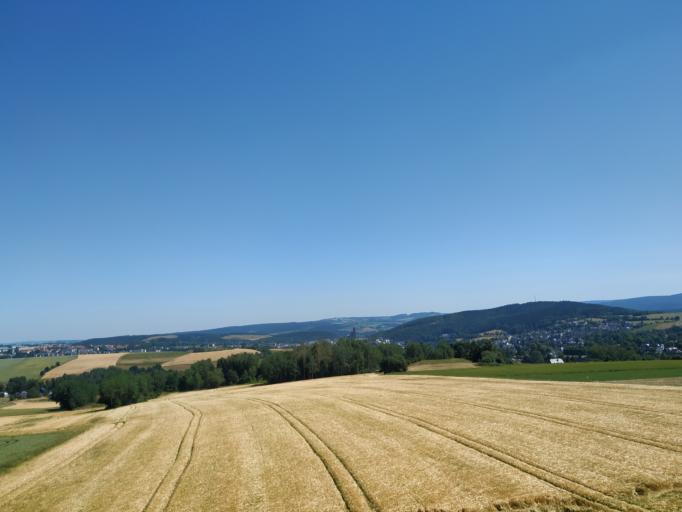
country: DE
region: Saxony
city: Schneeberg
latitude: 50.5794
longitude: 12.6154
